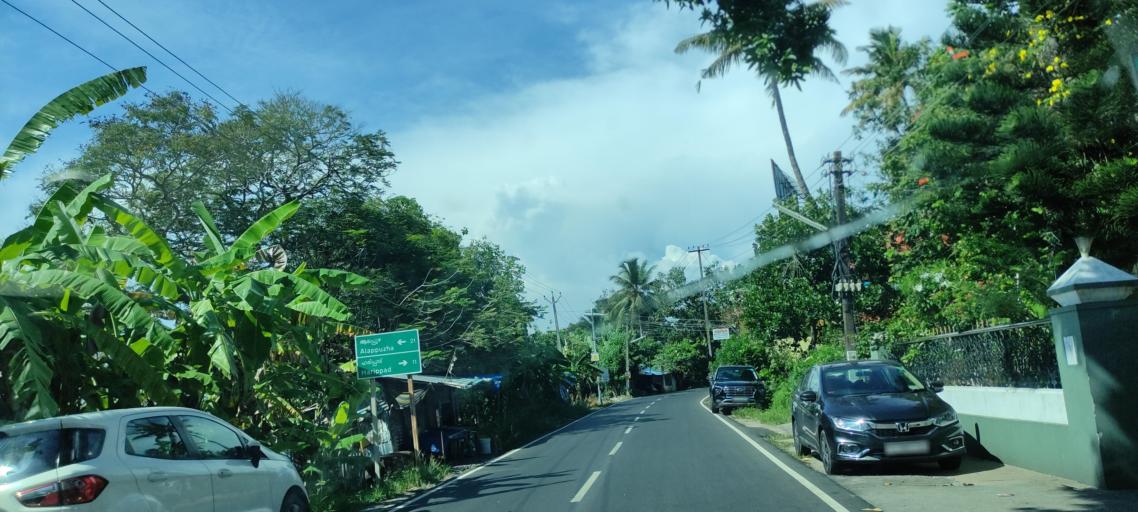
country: IN
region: Kerala
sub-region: Alappuzha
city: Mavelikara
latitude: 9.3150
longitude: 76.3870
